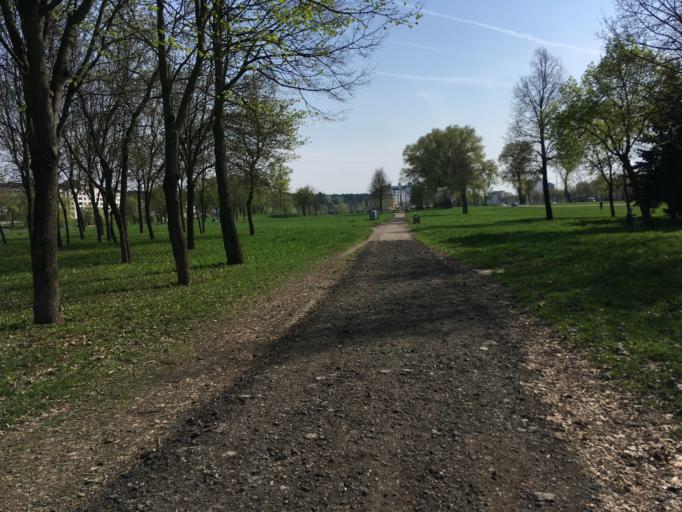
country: BY
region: Minsk
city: Minsk
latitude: 53.9239
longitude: 27.6400
